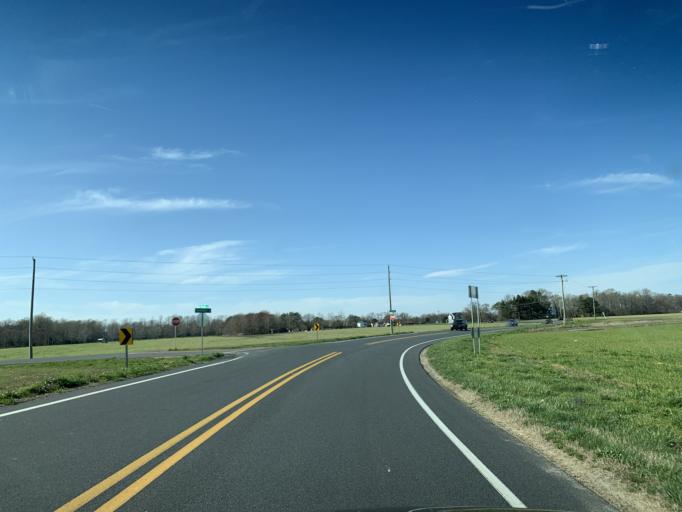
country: US
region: Delaware
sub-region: Sussex County
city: Milford
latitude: 38.9518
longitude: -75.4743
